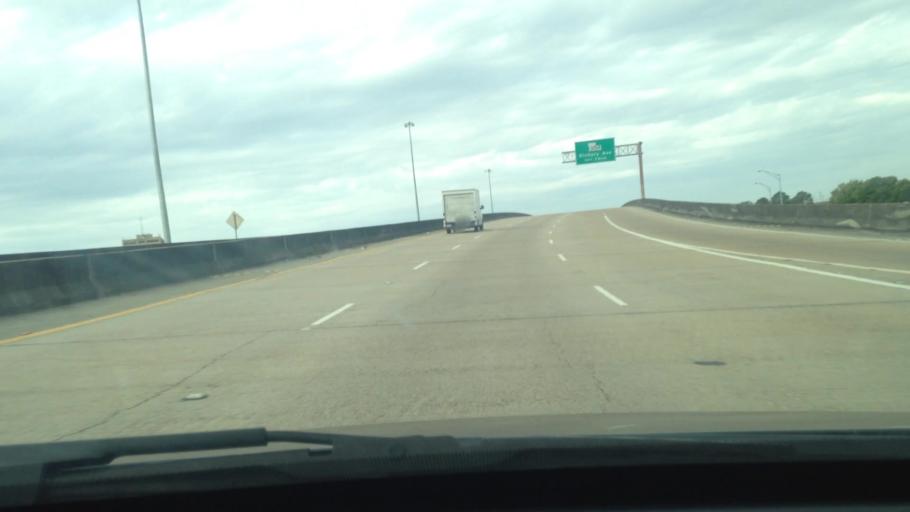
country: US
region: Louisiana
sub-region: Jefferson Parish
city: Elmwood
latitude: 29.9682
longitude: -90.1811
